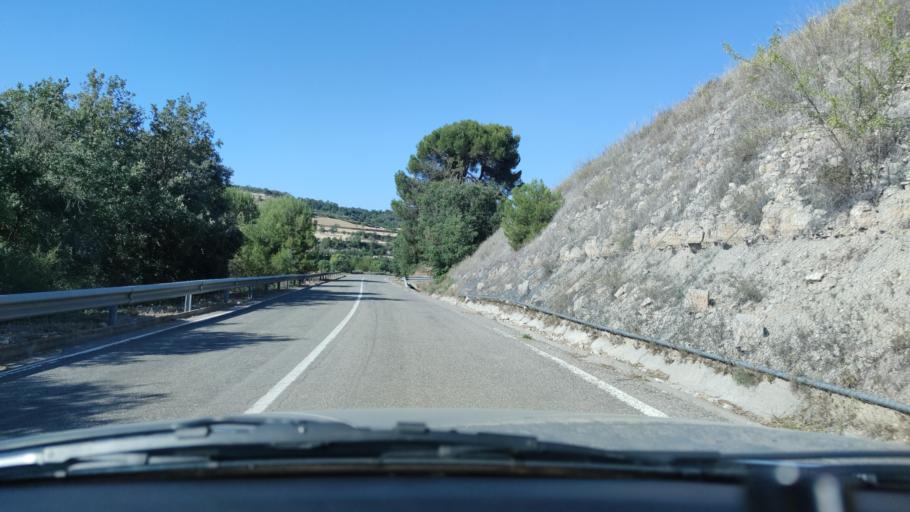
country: ES
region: Catalonia
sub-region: Provincia de Barcelona
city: Pujalt
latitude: 41.6969
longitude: 1.3589
